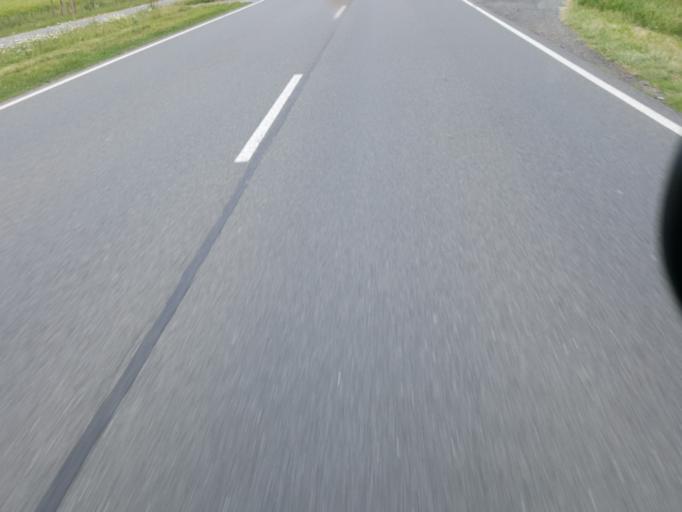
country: DE
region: Lower Saxony
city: Leese
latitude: 52.4886
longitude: 9.1269
